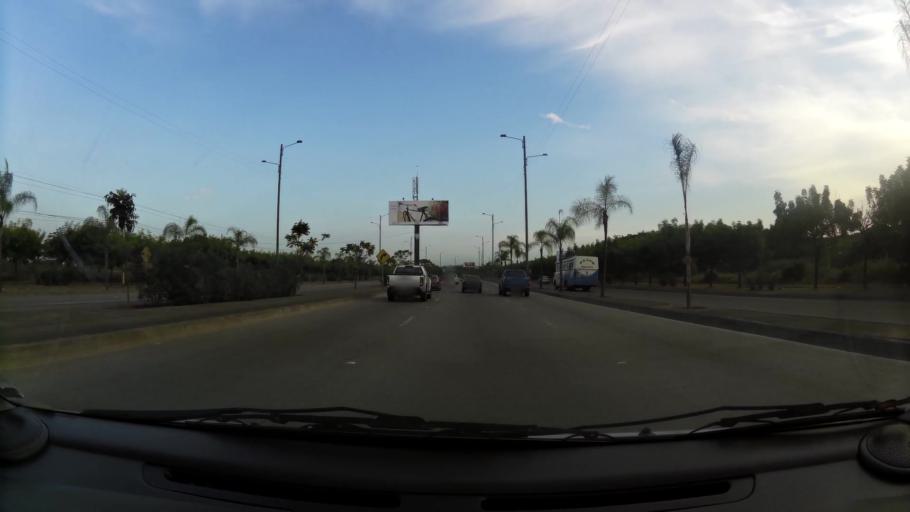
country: EC
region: Guayas
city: Eloy Alfaro
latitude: -2.0988
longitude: -79.8905
